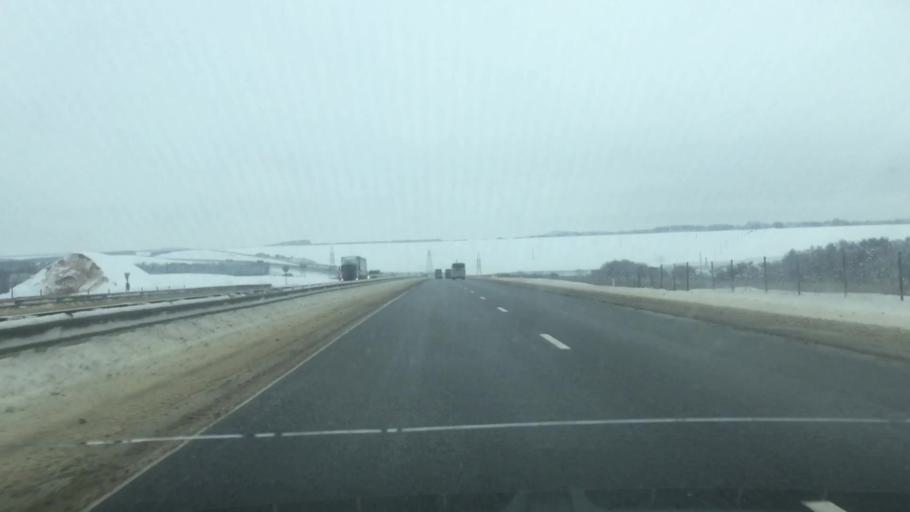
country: RU
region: Tula
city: Kazachka
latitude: 53.2829
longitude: 38.1793
